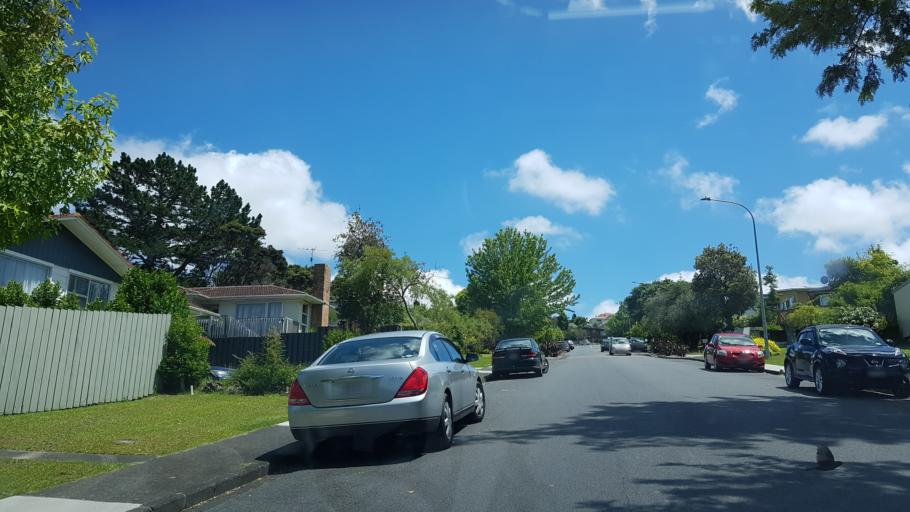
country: NZ
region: Auckland
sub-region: Auckland
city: North Shore
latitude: -36.7780
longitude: 174.7150
